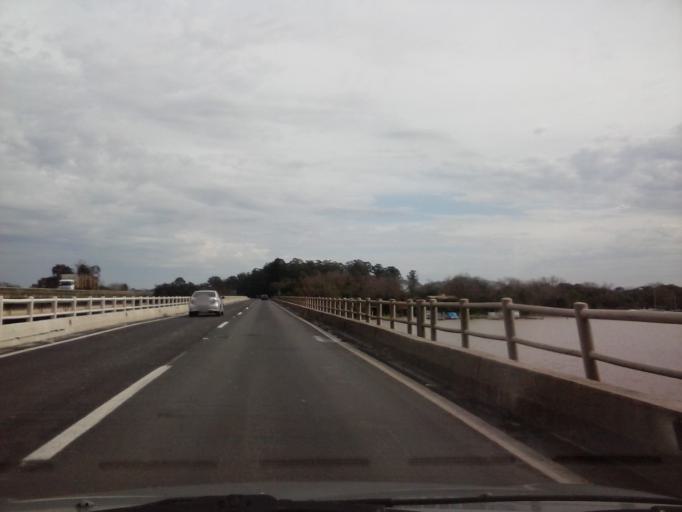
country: BR
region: Rio Grande do Sul
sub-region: Porto Alegre
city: Porto Alegre
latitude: -29.9879
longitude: -51.2379
